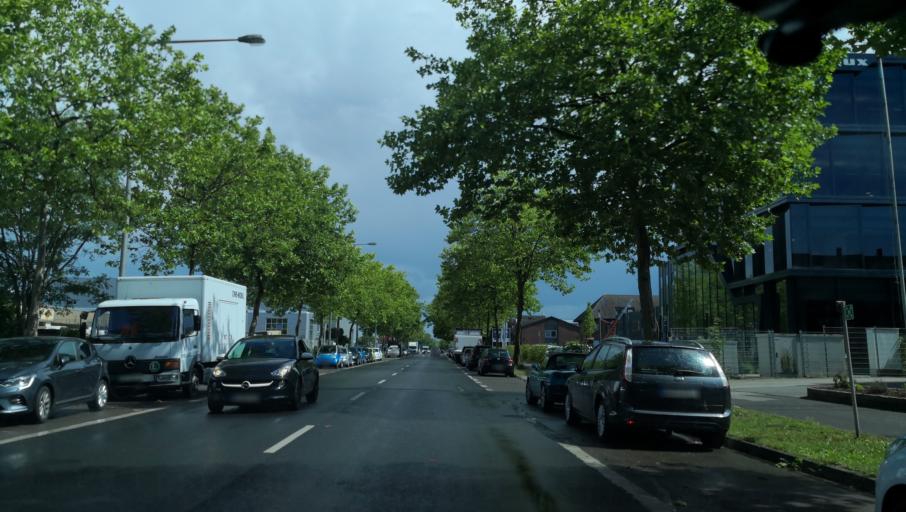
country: DE
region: North Rhine-Westphalia
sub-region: Regierungsbezirk Koln
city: Mengenich
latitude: 50.9857
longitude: 6.8822
